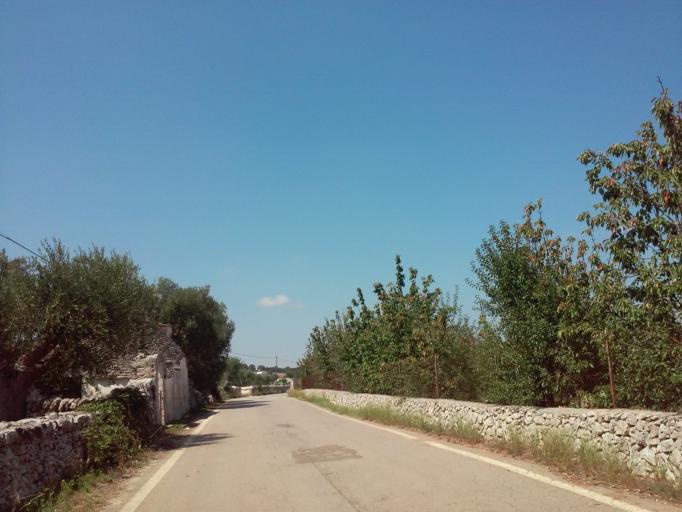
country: IT
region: Apulia
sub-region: Provincia di Bari
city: Alberobello
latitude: 40.7969
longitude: 17.2185
